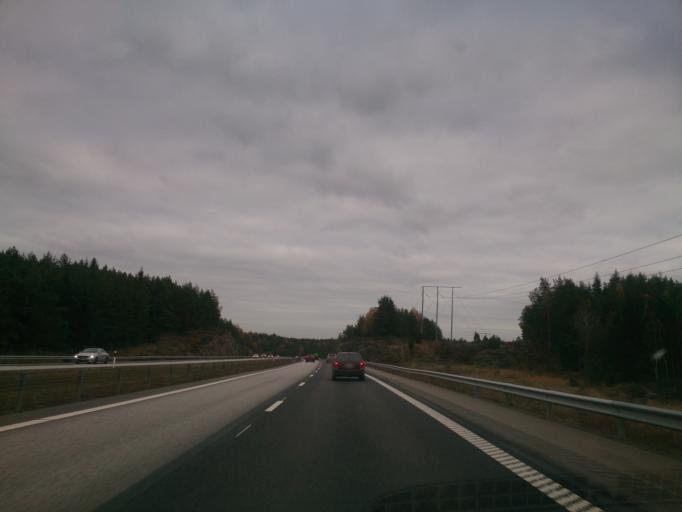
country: SE
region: Soedermanland
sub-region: Oxelosunds Kommun
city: Oxelosund
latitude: 58.8357
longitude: 17.1733
